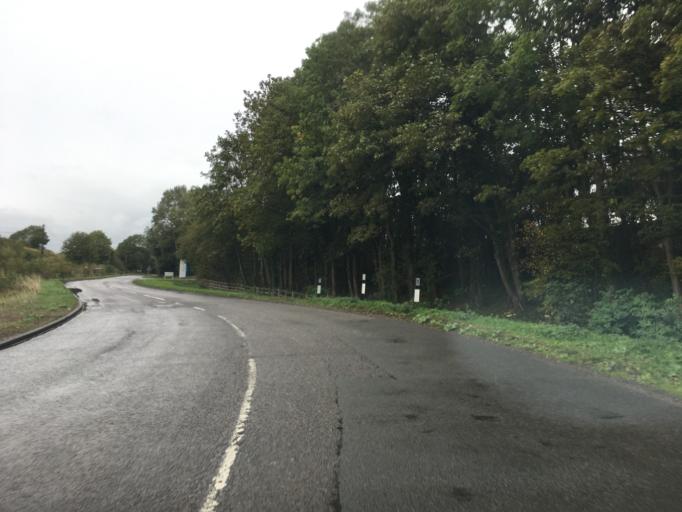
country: GB
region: England
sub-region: Nottinghamshire
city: East Leake
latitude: 52.8499
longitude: -1.1789
